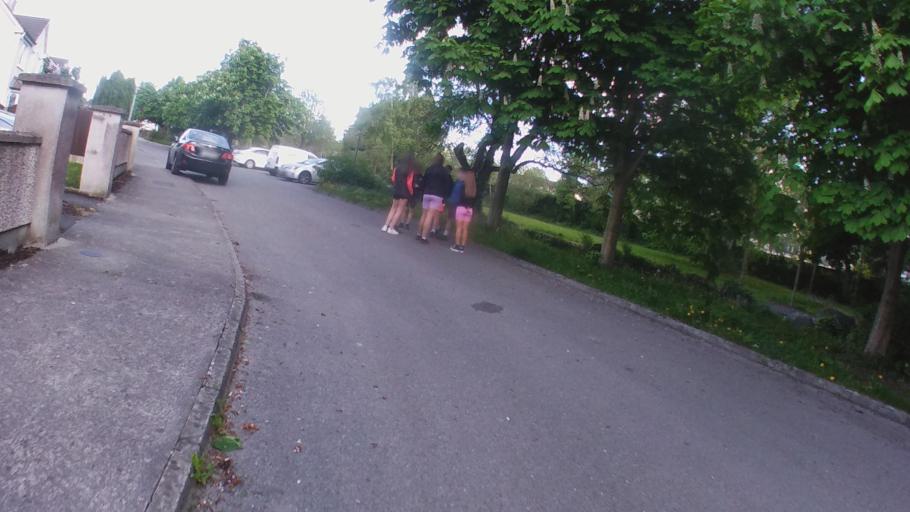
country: IE
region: Leinster
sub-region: County Carlow
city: Carlow
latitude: 52.8417
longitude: -6.9322
